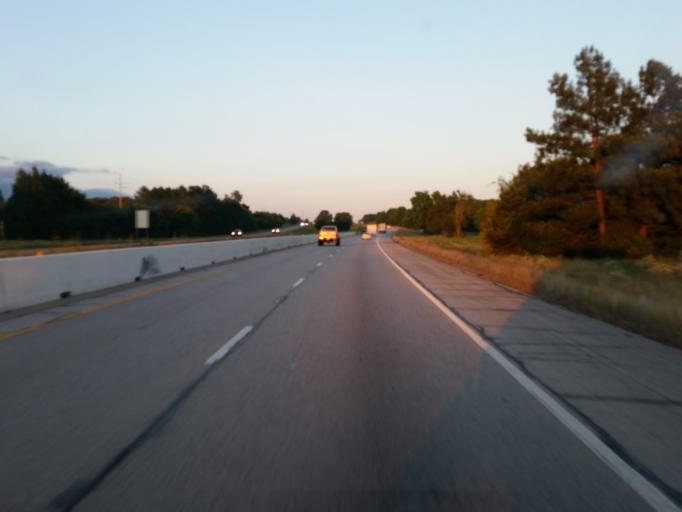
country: US
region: Texas
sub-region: Smith County
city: Hideaway
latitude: 32.4812
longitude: -95.5033
